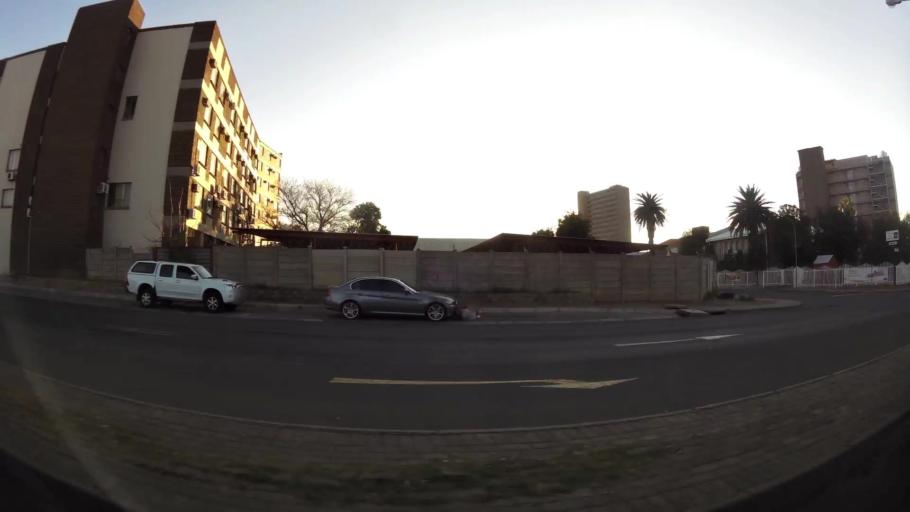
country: ZA
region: Northern Cape
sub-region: Frances Baard District Municipality
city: Kimberley
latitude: -28.7396
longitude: 24.7683
